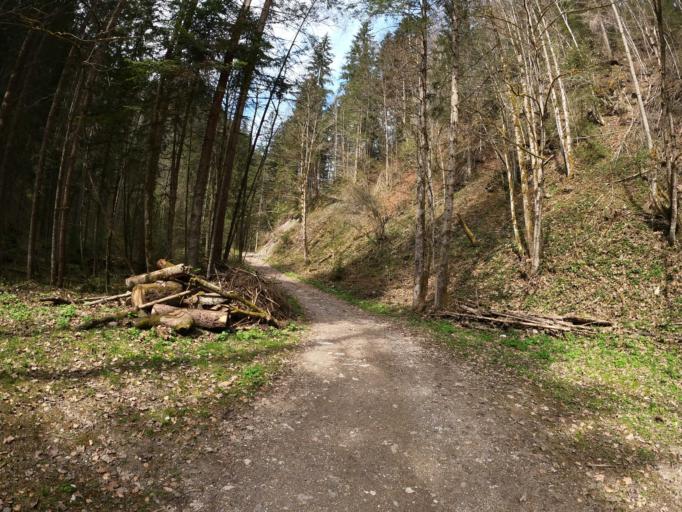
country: AT
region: Salzburg
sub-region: Politischer Bezirk Sankt Johann im Pongau
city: Pfarrwerfen
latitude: 47.4593
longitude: 13.2258
